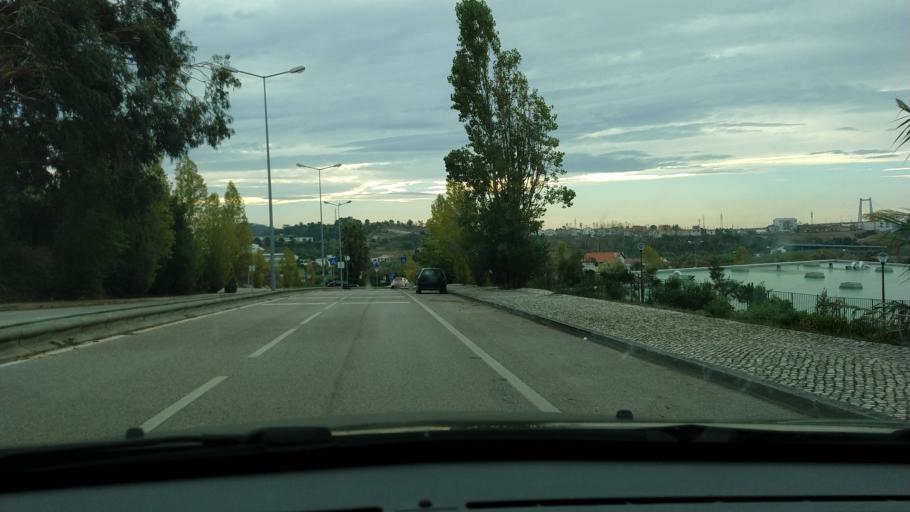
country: PT
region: Coimbra
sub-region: Figueira da Foz
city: Figueira da Foz
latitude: 40.1582
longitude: -8.8506
